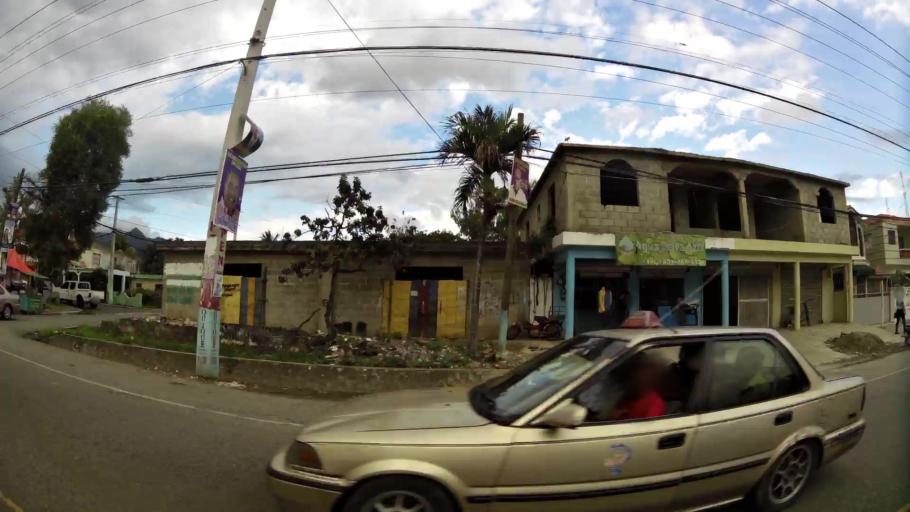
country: DO
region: San Cristobal
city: Villa Altagracia
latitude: 18.6813
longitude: -70.1784
